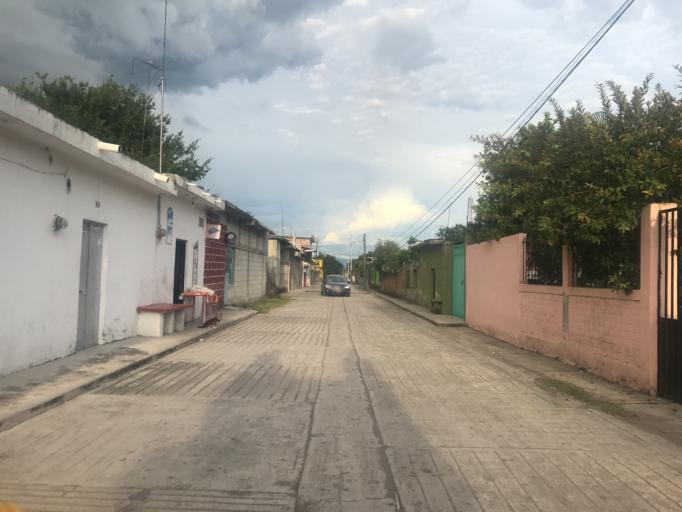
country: MX
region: Morelos
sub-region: Axochiapan
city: Quebrantadero
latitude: 18.5215
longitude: -98.7927
